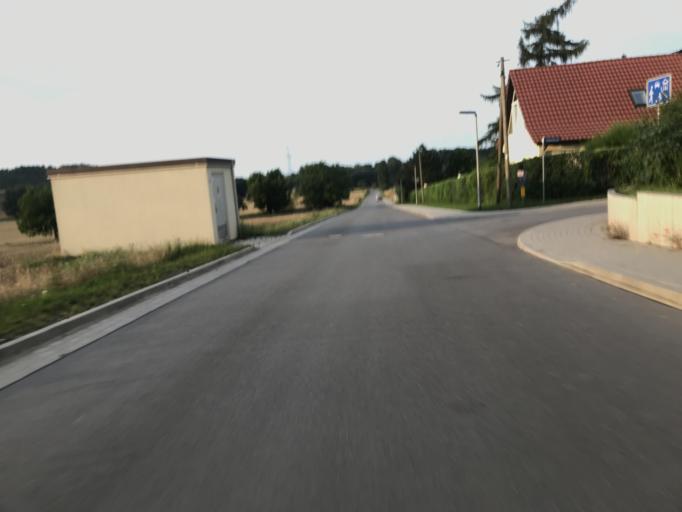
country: DE
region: Saxony-Anhalt
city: Quedlinburg
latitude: 51.8013
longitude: 11.1607
